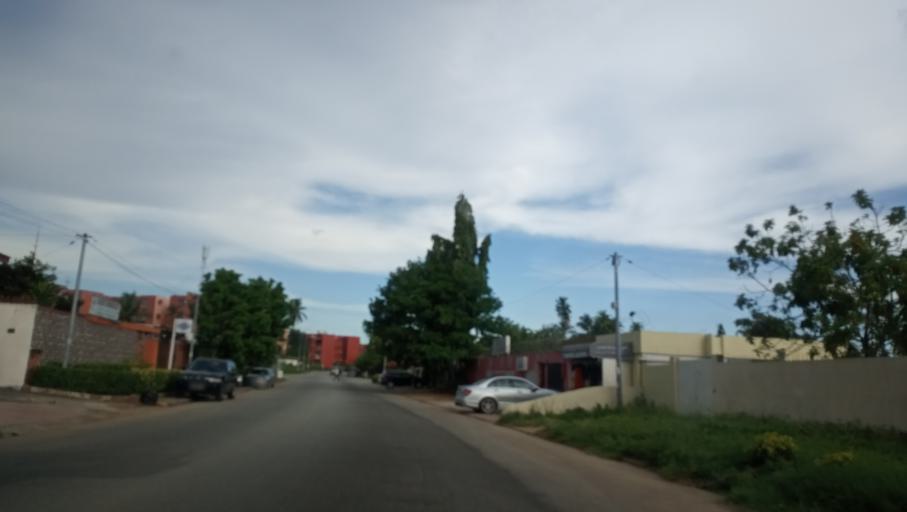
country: CI
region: Lagunes
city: Abidjan
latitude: 5.3444
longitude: -3.9801
